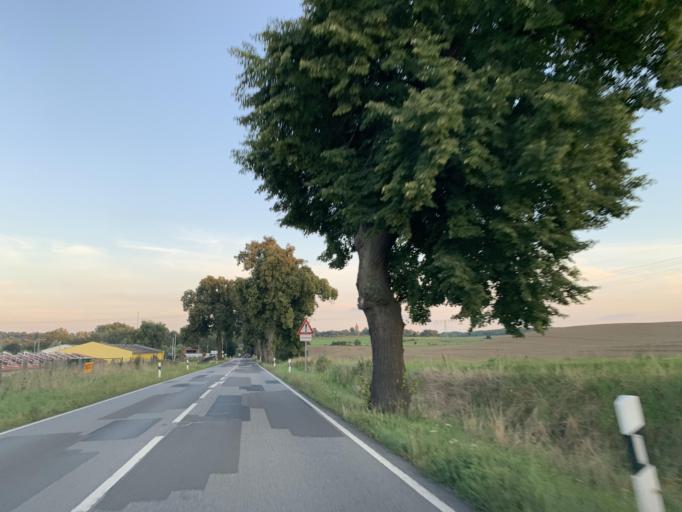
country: DE
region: Mecklenburg-Vorpommern
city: Burg Stargard
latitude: 53.5048
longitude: 13.2950
